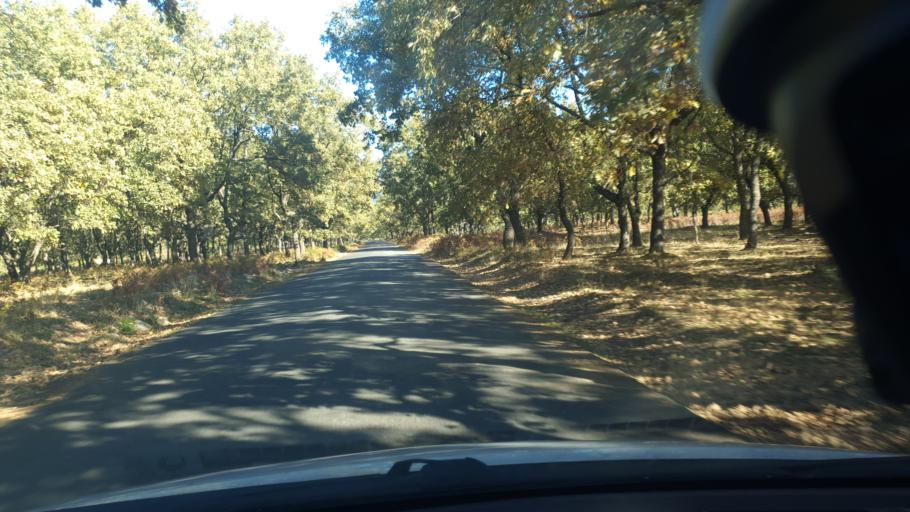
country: ES
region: Castille and Leon
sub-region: Provincia de Avila
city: Candeleda
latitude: 40.1362
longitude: -5.2616
